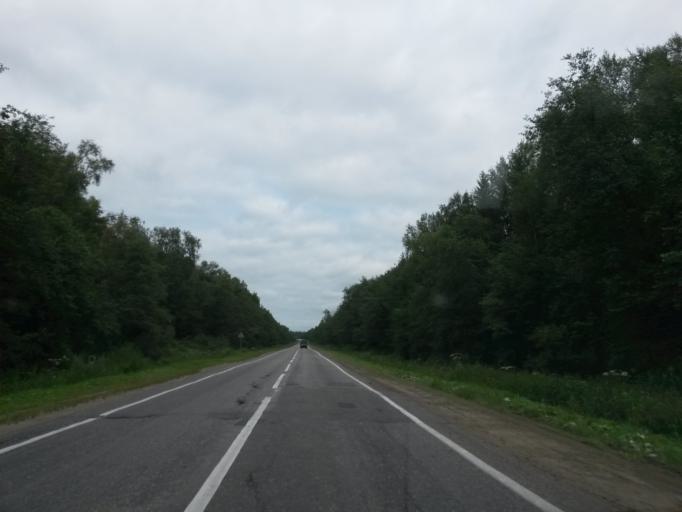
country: RU
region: Jaroslavl
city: Gavrilov-Yam
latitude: 57.4314
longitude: 39.9184
